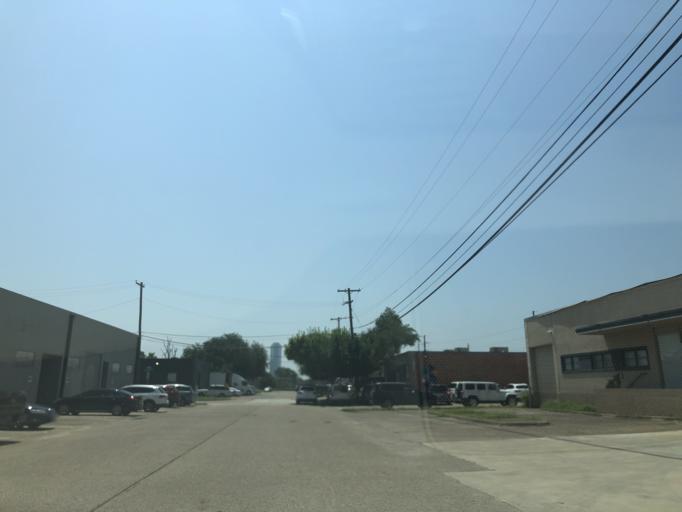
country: US
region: Texas
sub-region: Dallas County
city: Dallas
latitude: 32.7998
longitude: -96.8391
